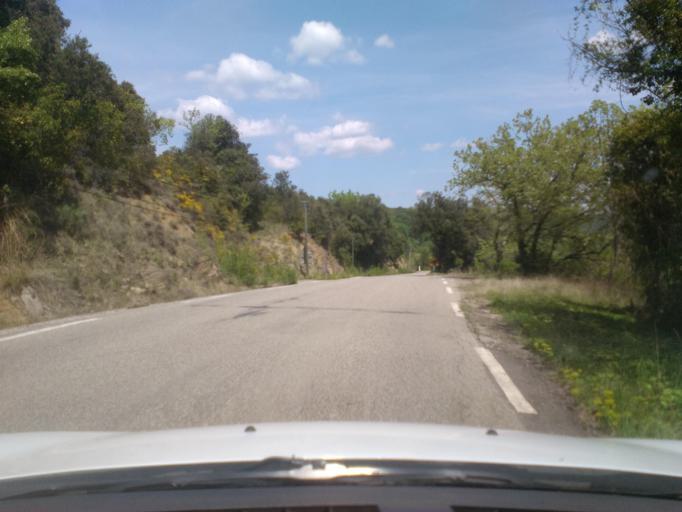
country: FR
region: Languedoc-Roussillon
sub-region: Departement du Gard
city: Saint-Hippolyte-du-Fort
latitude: 43.9833
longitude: 3.8838
